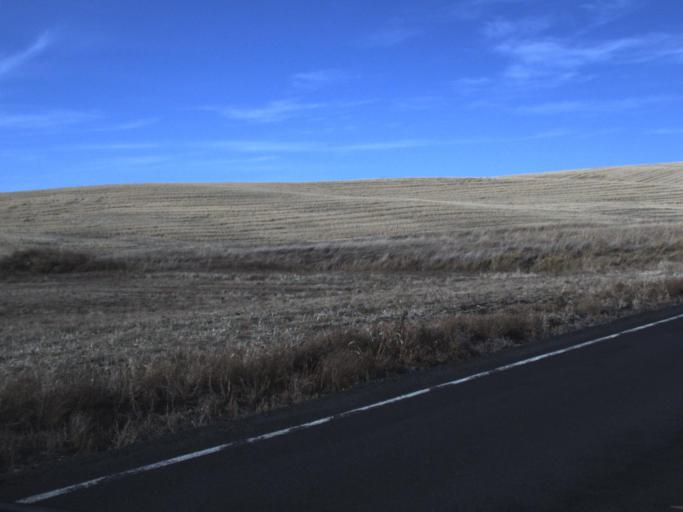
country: US
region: Washington
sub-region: Lincoln County
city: Davenport
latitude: 47.7156
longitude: -118.1515
